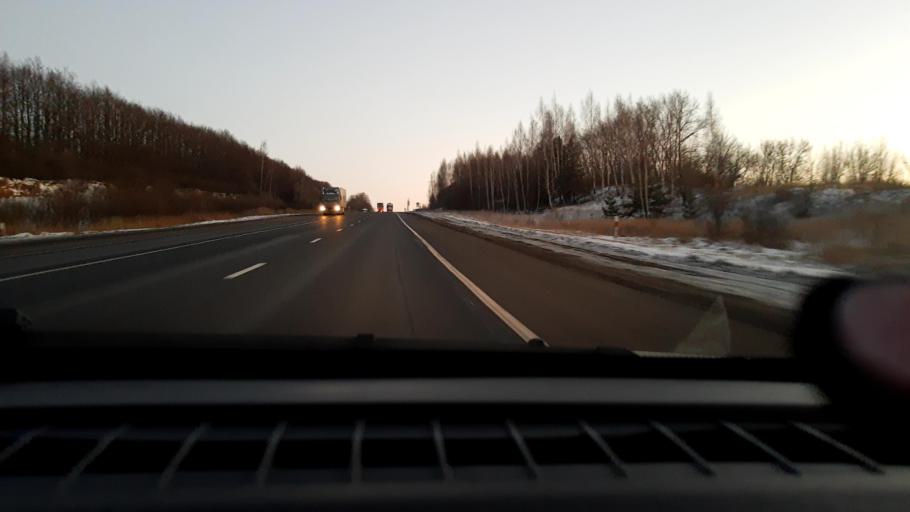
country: RU
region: Nizjnij Novgorod
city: Pervoye Maya
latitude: 55.9972
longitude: 44.7517
